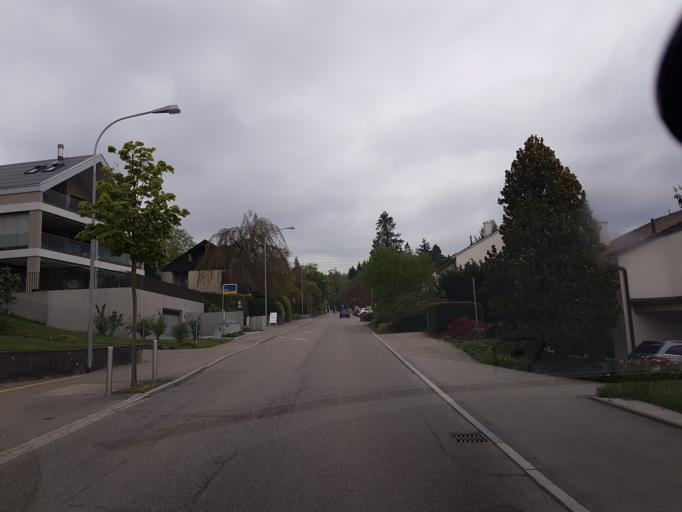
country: CH
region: Zurich
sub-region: Bezirk Dietikon
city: Uitikon
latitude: 47.3690
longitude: 8.4594
